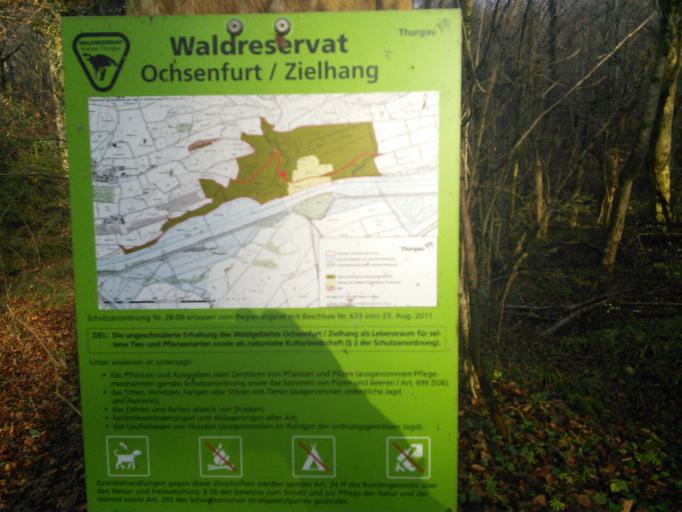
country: CH
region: Thurgau
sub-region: Frauenfeld District
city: Frauenfeld
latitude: 47.5882
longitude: 8.9126
